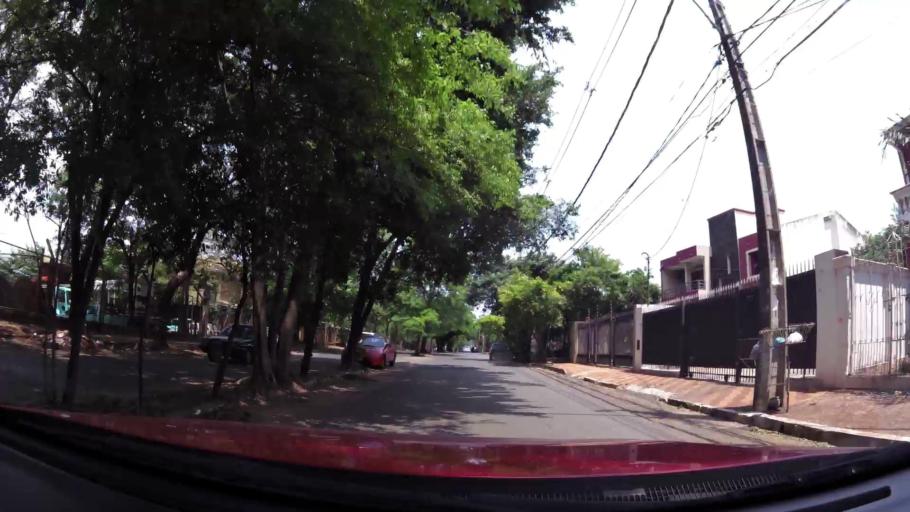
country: PY
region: Central
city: Lambare
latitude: -25.3091
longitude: -57.5680
